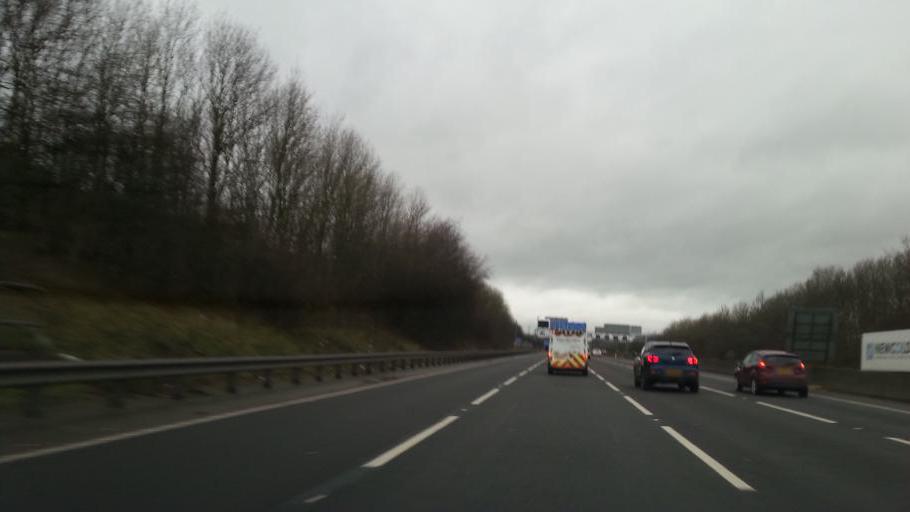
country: GB
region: England
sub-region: City and Borough of Leeds
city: Lofthouse
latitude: 53.7282
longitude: -1.4701
